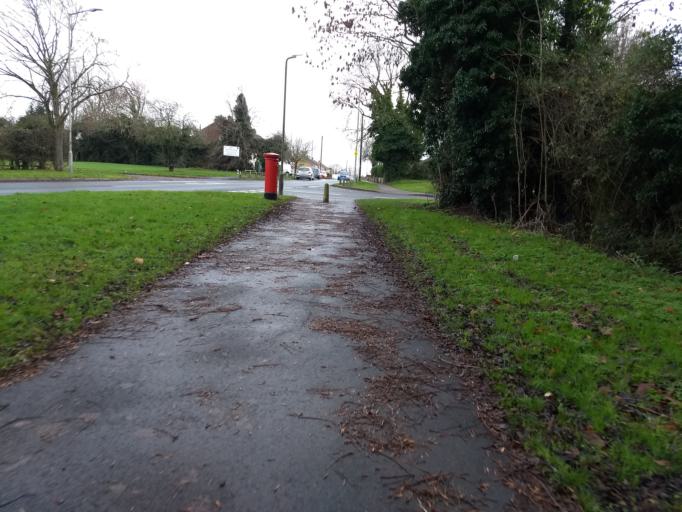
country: GB
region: England
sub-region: Buckinghamshire
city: Newton Longville
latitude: 51.9949
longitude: -0.7659
